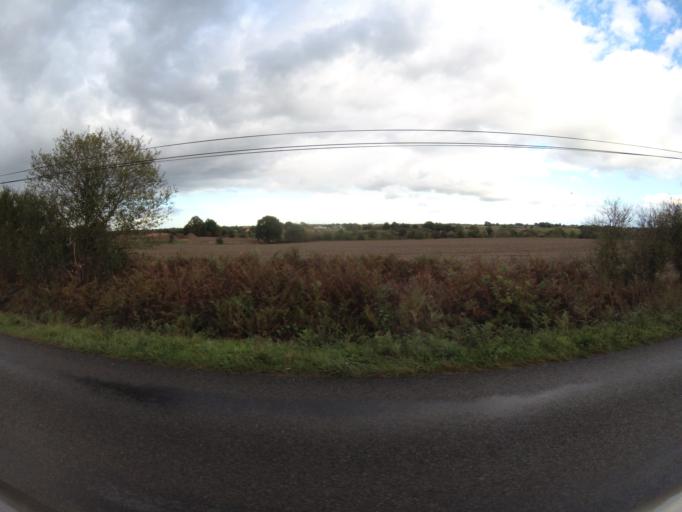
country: FR
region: Pays de la Loire
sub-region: Departement de la Loire-Atlantique
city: Saint-Hilaire-de-Clisson
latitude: 47.0701
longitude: -1.3238
